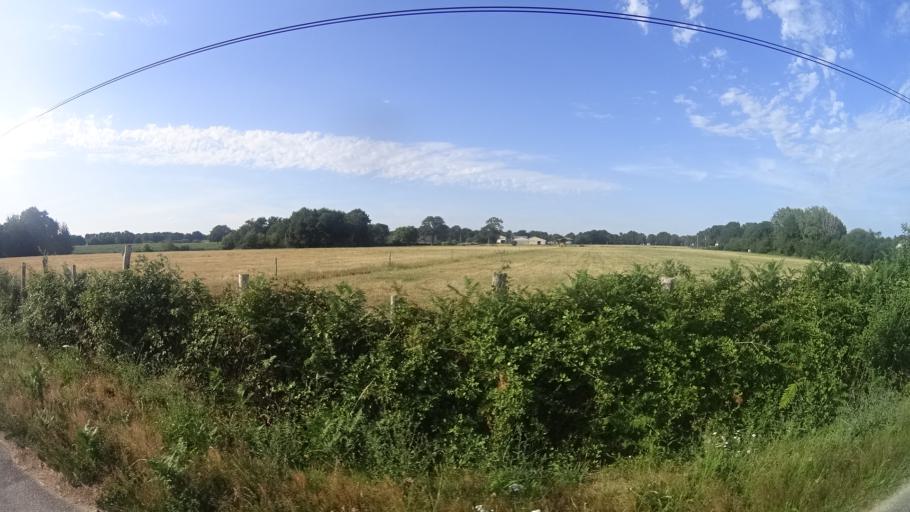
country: FR
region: Brittany
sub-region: Departement du Morbihan
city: Saint-Jean-la-Poterie
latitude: 47.6411
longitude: -2.1400
